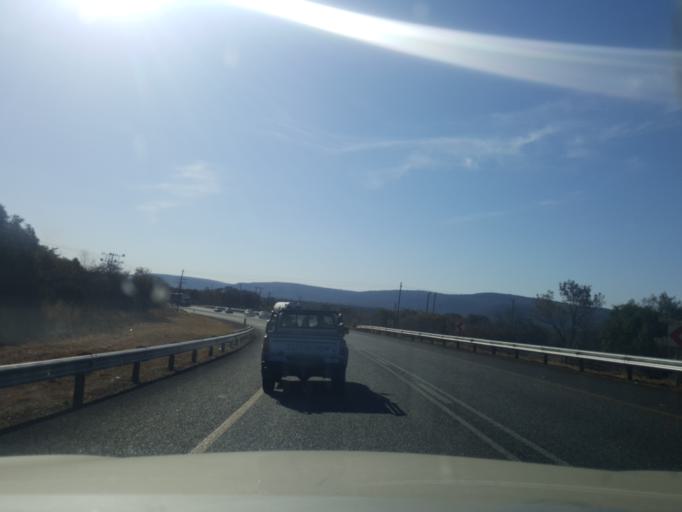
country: ZA
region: North-West
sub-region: Ngaka Modiri Molema District Municipality
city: Zeerust
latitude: -25.5291
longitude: 26.1904
